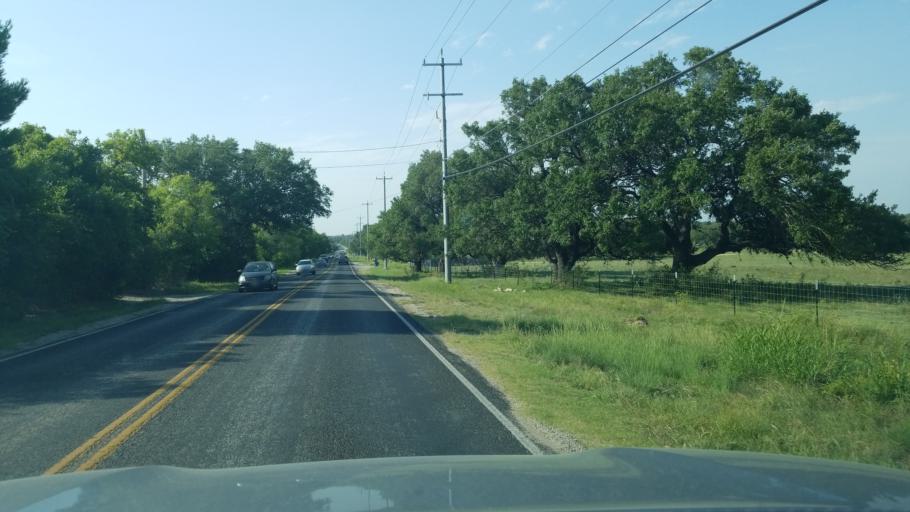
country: US
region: Texas
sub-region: Bexar County
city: Helotes
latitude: 29.4531
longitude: -98.7551
